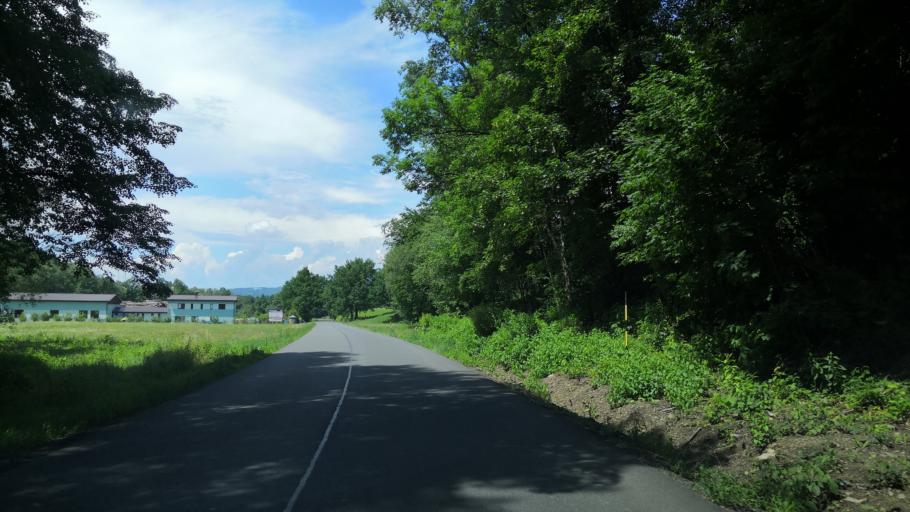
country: CZ
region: Zlin
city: Vidce
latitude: 49.4507
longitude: 18.0760
